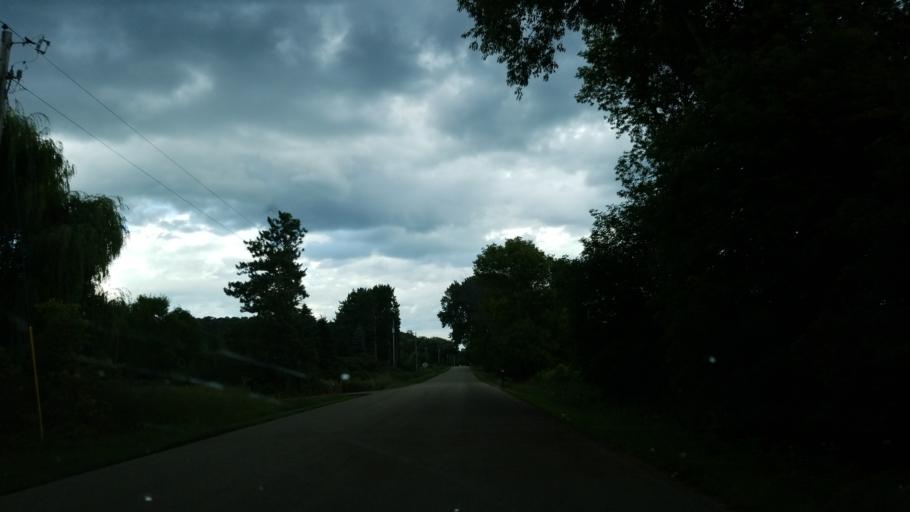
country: US
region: Minnesota
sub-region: Washington County
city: Lake Saint Croix Beach
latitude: 44.8802
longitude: -92.7386
